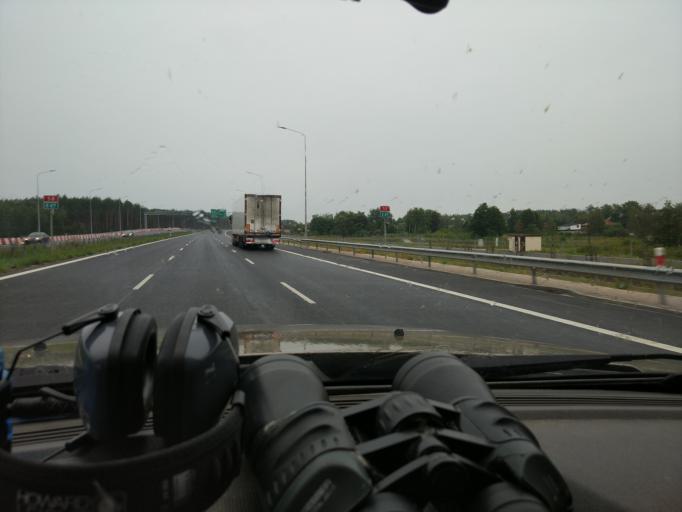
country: PL
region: Masovian Voivodeship
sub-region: Powiat wolominski
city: Slupno
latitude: 52.3736
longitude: 21.1885
